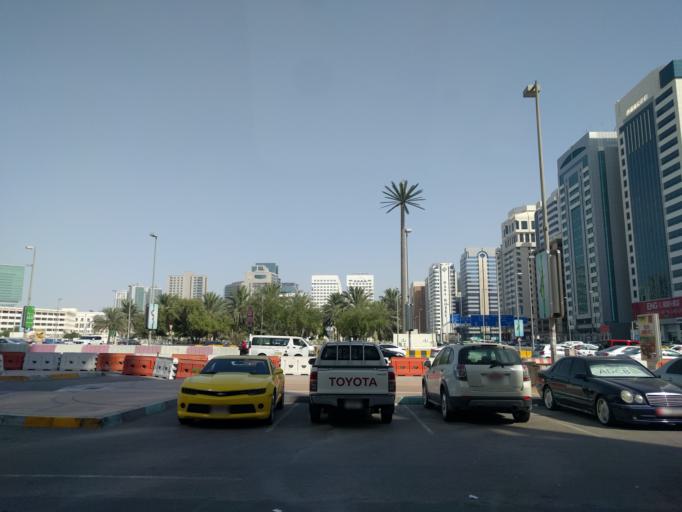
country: AE
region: Abu Dhabi
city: Abu Dhabi
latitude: 24.5003
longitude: 54.3775
